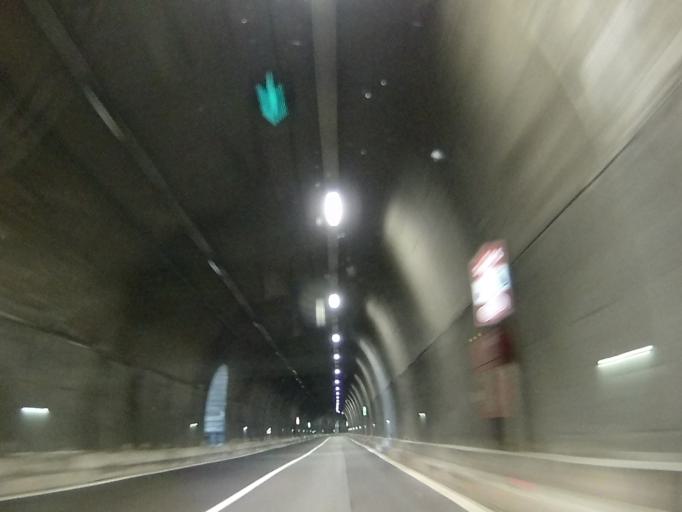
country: IT
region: Lombardy
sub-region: Provincia di Brescia
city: Limone sul Garda
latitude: 45.7921
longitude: 10.7800
